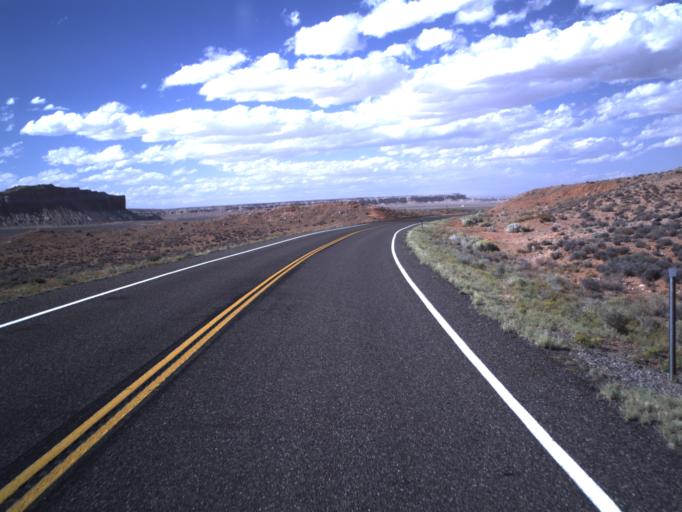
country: US
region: Utah
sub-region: Wayne County
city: Loa
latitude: 38.1493
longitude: -110.6190
